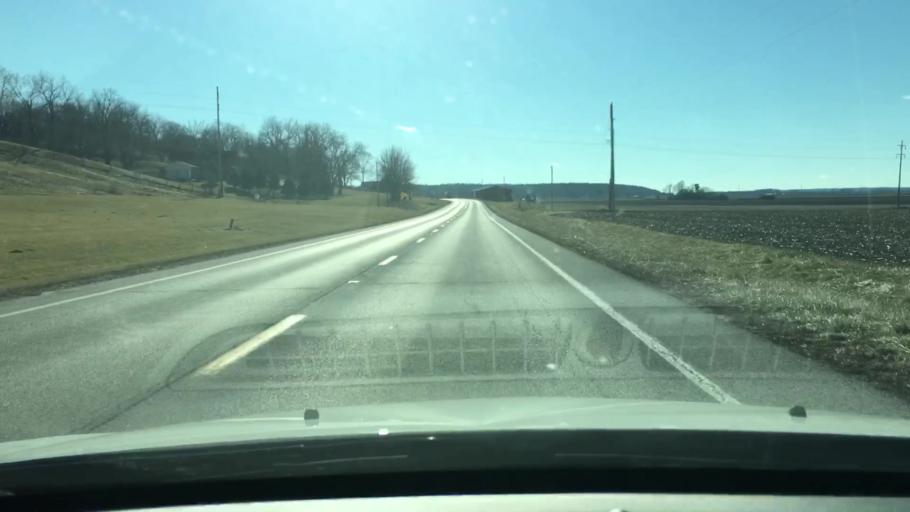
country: US
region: Illinois
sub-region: Morgan County
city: Meredosia
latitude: 39.7699
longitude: -90.5320
